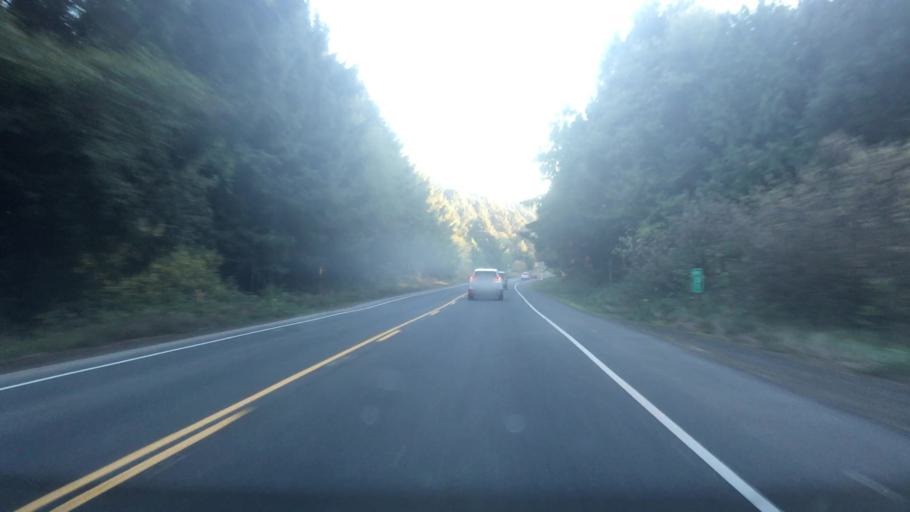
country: US
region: Oregon
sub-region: Clatsop County
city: Cannon Beach
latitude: 45.8669
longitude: -123.9587
